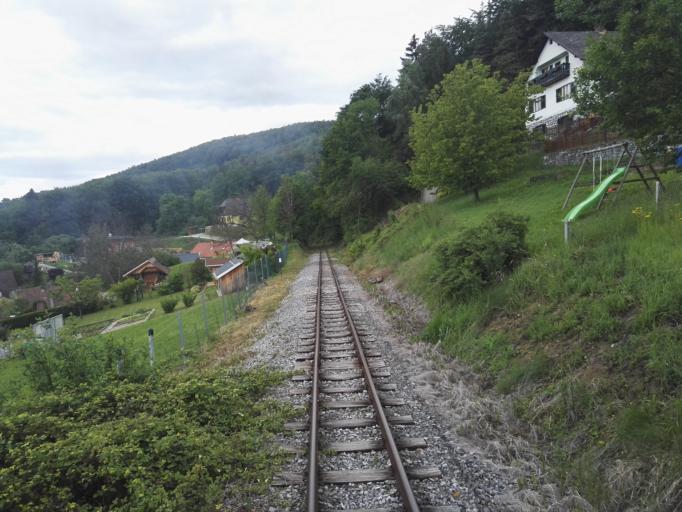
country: AT
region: Styria
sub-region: Politischer Bezirk Weiz
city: Puch bei Weiz
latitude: 47.2304
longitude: 15.6759
